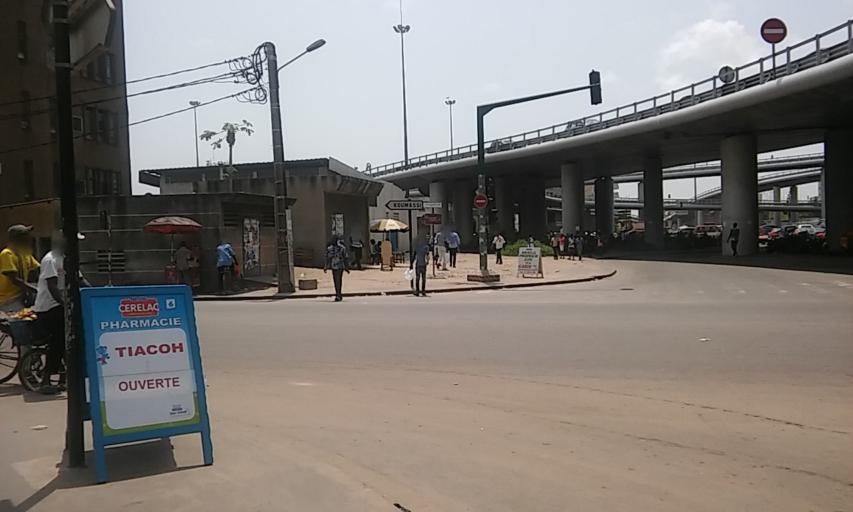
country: CI
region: Lagunes
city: Abidjan
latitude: 5.2971
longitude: -3.9809
